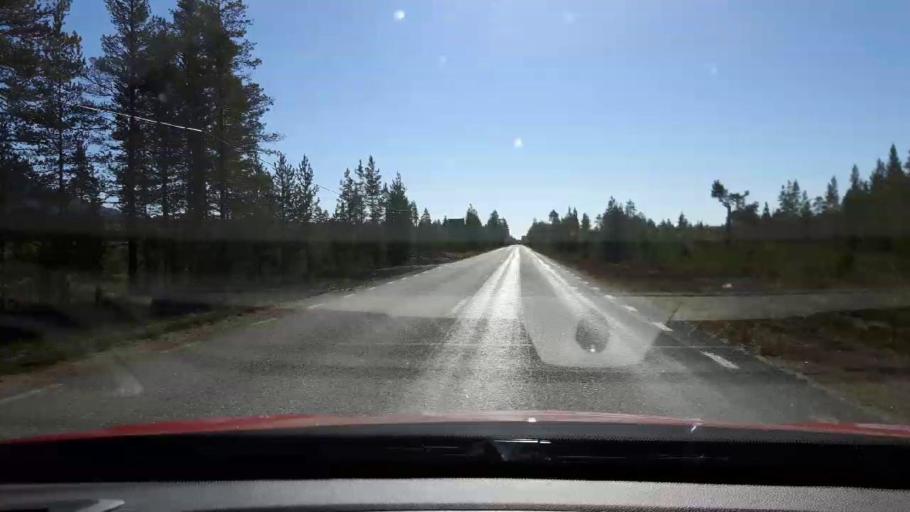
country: SE
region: Jaemtland
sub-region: Harjedalens Kommun
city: Sveg
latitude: 62.4099
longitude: 13.9215
